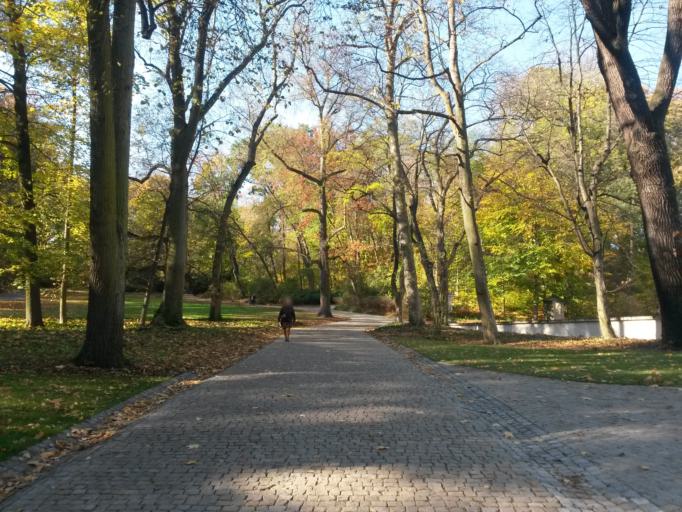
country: PL
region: Masovian Voivodeship
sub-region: Warszawa
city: Srodmiescie
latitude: 52.2157
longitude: 21.0300
